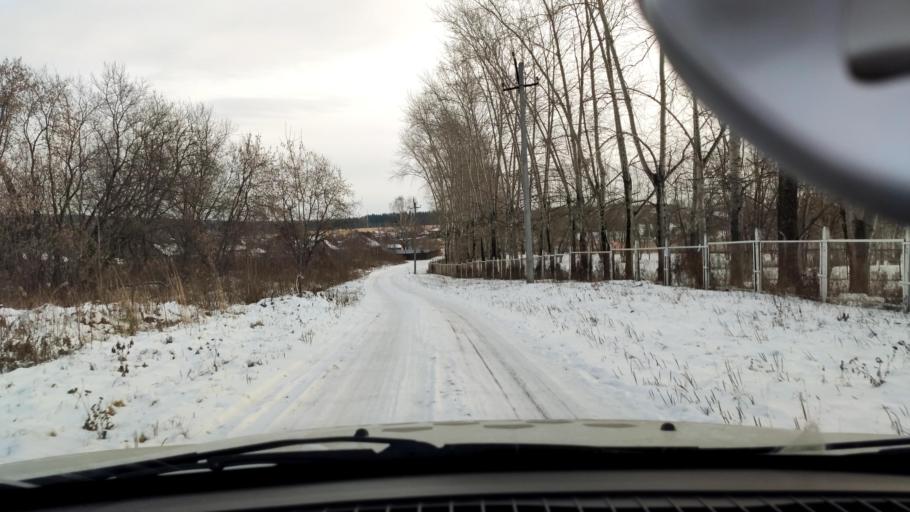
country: RU
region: Perm
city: Lobanovo
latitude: 57.8267
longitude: 56.3508
